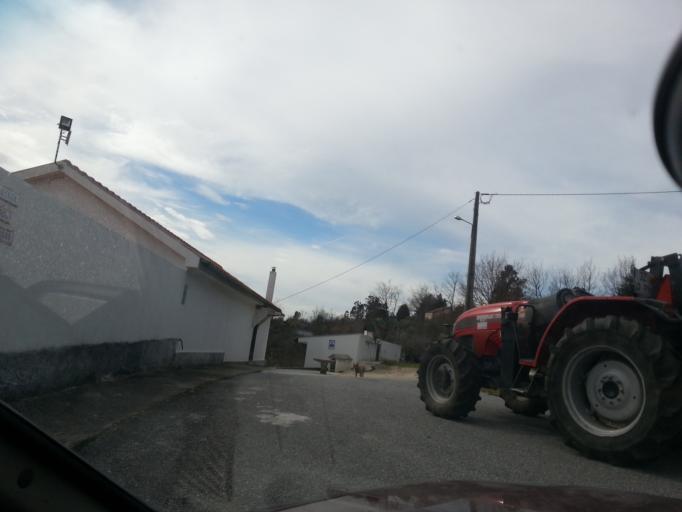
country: PT
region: Guarda
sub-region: Fornos de Algodres
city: Fornos de Algodres
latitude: 40.6056
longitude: -7.5442
